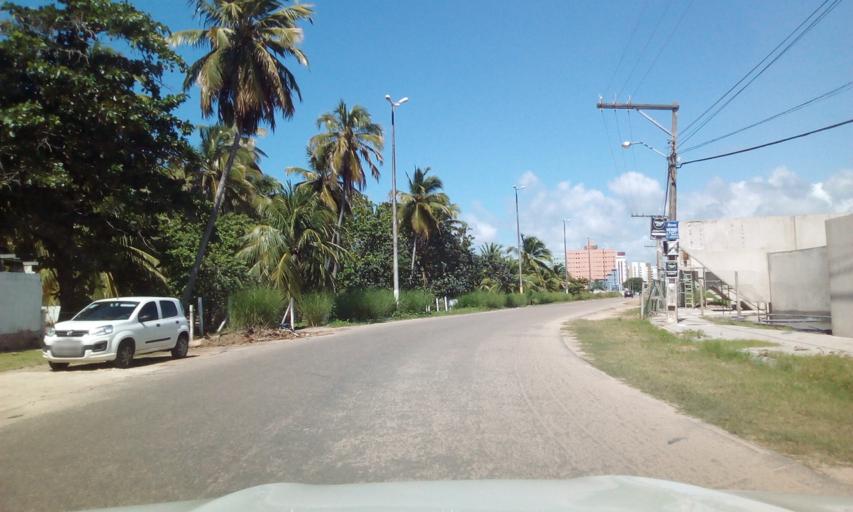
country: BR
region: Paraiba
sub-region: Cabedelo
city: Cabedelo
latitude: -7.0262
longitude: -34.8307
